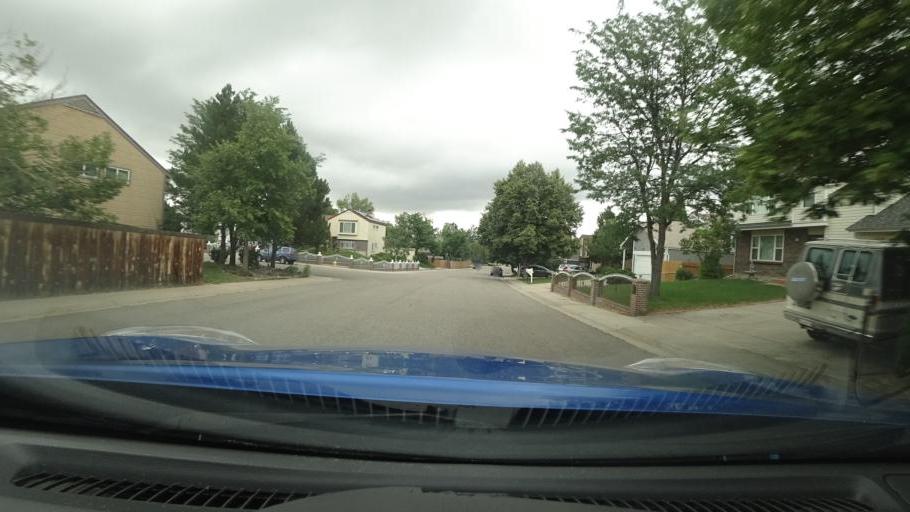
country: US
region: Colorado
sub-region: Adams County
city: Aurora
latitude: 39.7008
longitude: -104.8131
